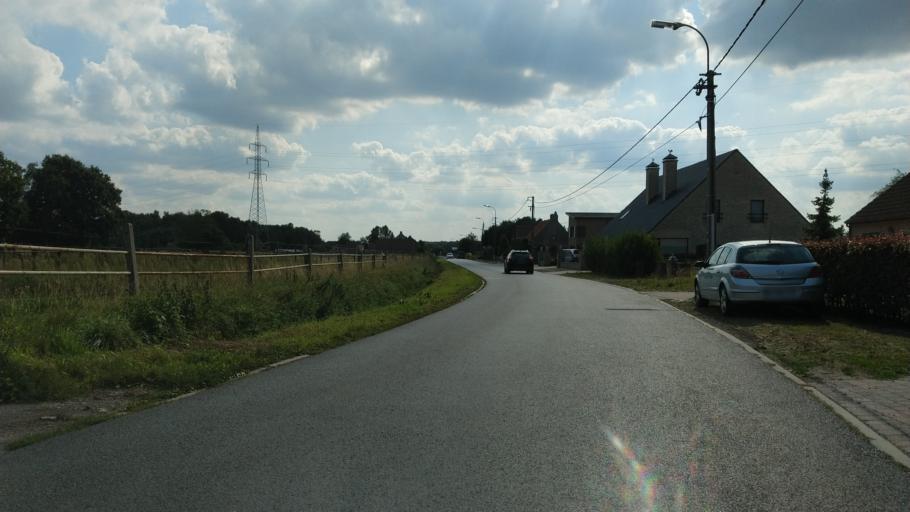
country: BE
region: Flanders
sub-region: Provincie Oost-Vlaanderen
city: Kaprijke
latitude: 51.1848
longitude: 3.6801
